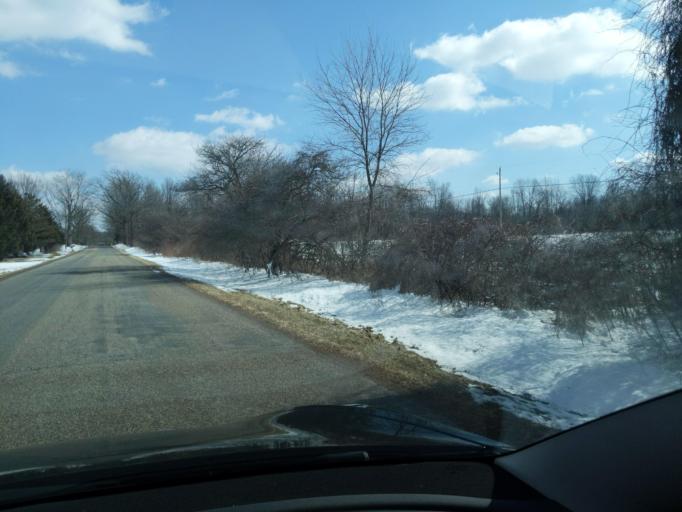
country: US
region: Michigan
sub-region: Ingham County
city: Mason
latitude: 42.6108
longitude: -84.3706
